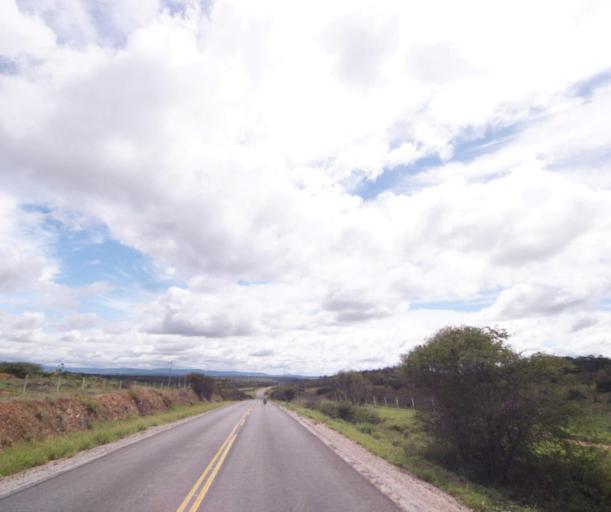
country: BR
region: Bahia
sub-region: Brumado
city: Brumado
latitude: -14.1543
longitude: -41.5148
